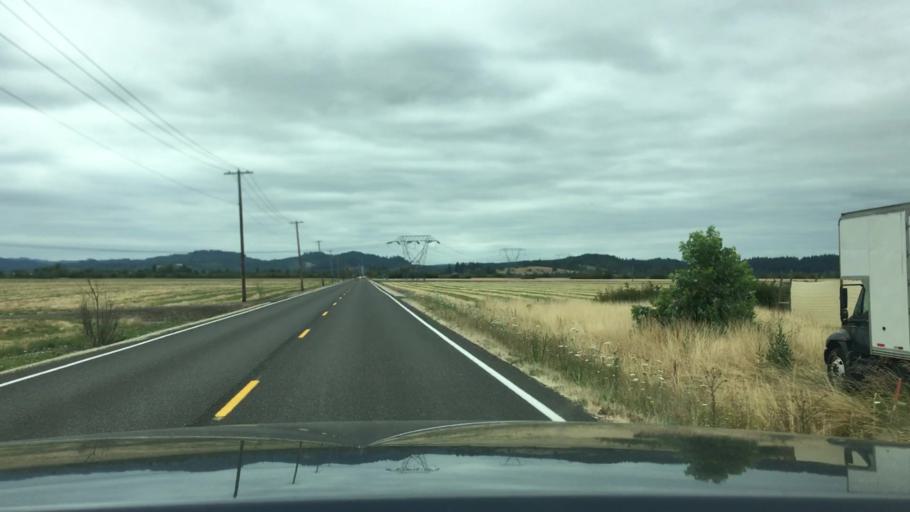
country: US
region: Oregon
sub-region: Lane County
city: Junction City
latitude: 44.0960
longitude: -123.2084
